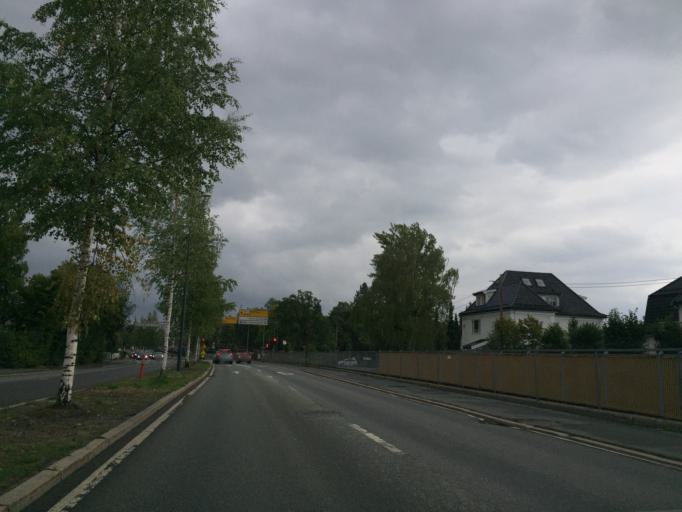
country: NO
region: Oslo
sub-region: Oslo
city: Sjolyststranda
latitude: 59.9354
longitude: 10.6920
